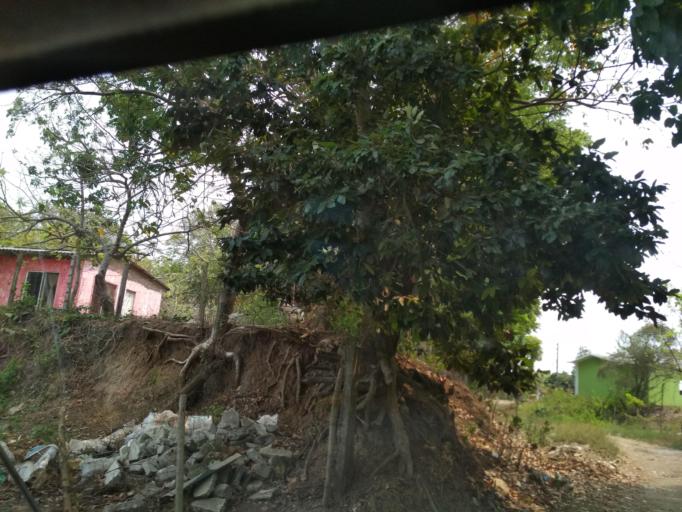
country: MX
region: Veracruz
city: El Tejar
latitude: 19.0685
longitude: -96.1532
